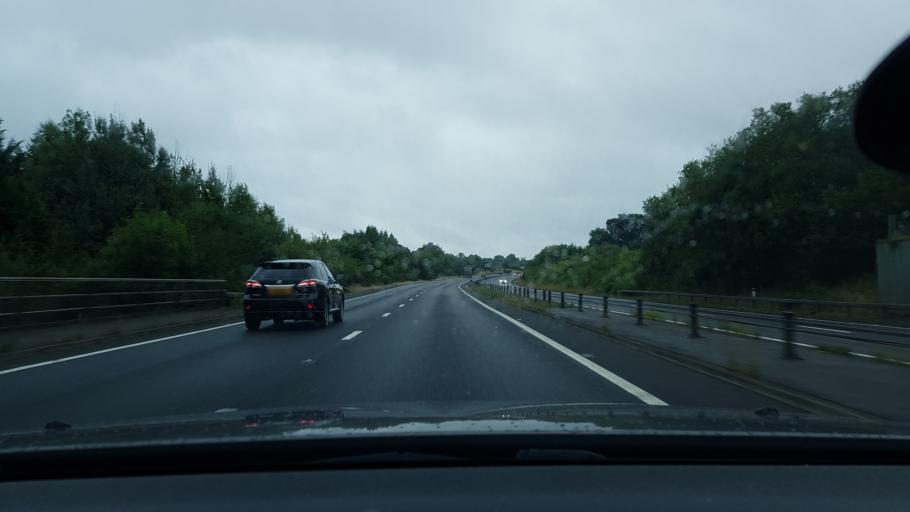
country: GB
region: England
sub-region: West Berkshire
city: Winterbourne
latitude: 51.4190
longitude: -1.3465
